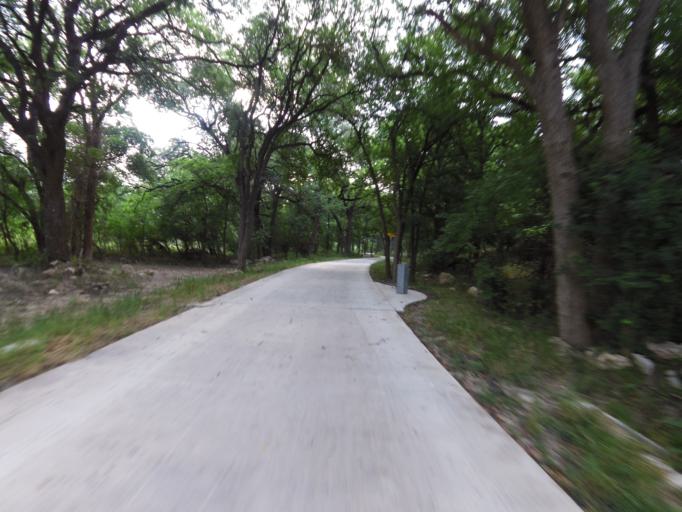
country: US
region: Texas
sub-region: Bexar County
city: Shavano Park
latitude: 29.5929
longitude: -98.6023
